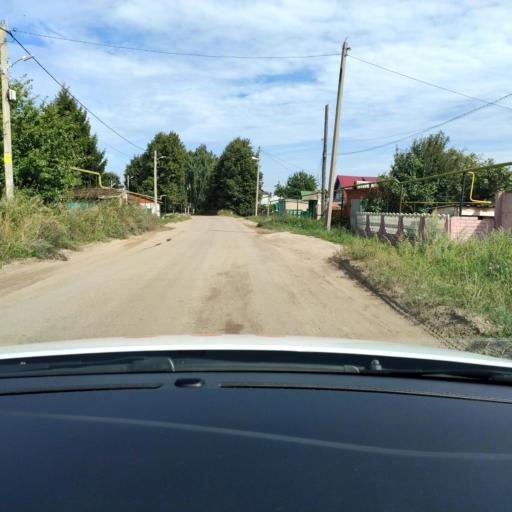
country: RU
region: Tatarstan
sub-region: Gorod Kazan'
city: Kazan
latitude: 55.7157
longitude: 49.0902
